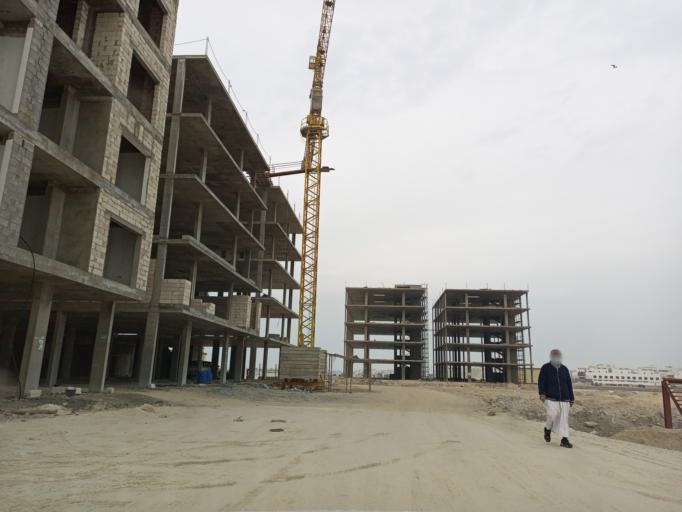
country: BH
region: Muharraq
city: Al Hadd
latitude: 26.2301
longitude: 50.6423
